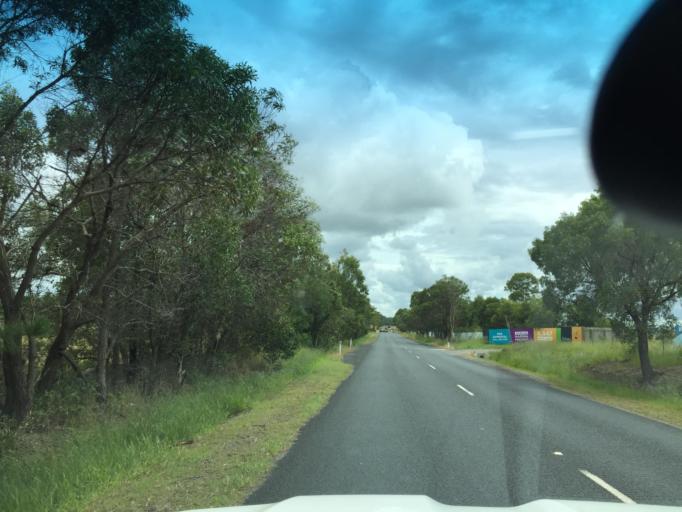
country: AU
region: Queensland
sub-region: Moreton Bay
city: Morayfield
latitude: -27.1132
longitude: 152.9800
